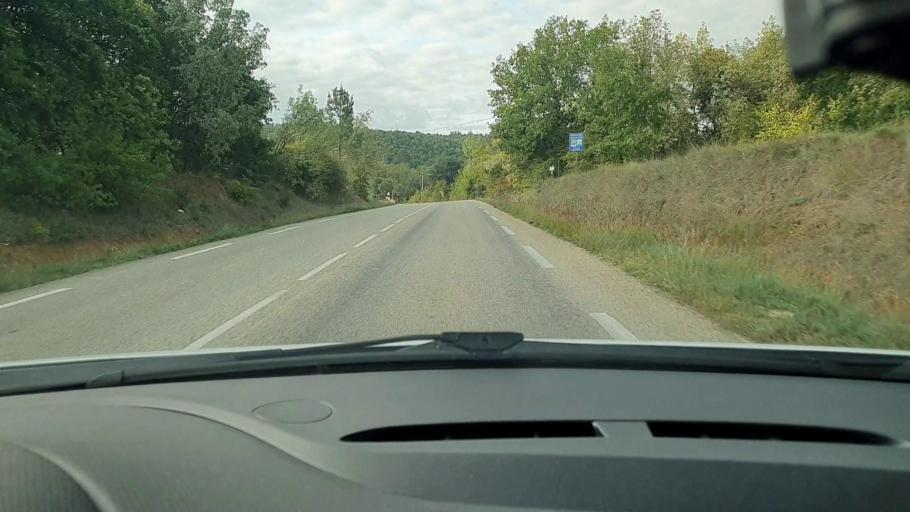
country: FR
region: Languedoc-Roussillon
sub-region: Departement du Gard
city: Saint-Ambroix
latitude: 44.2181
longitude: 4.2638
